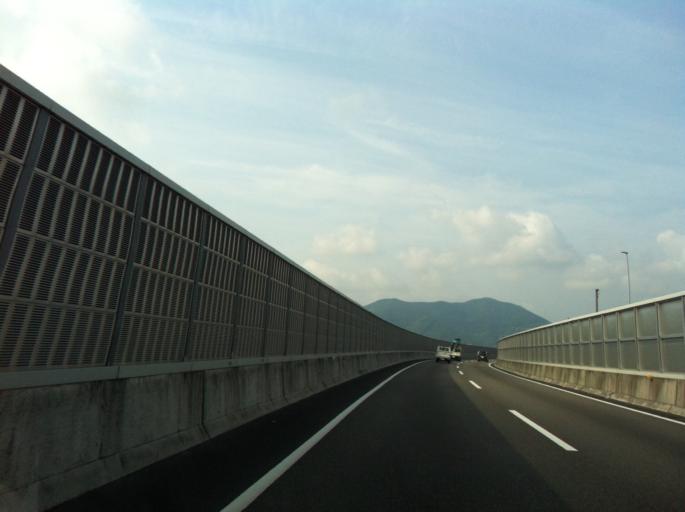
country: JP
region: Shizuoka
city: Shizuoka-shi
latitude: 34.9935
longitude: 138.3653
